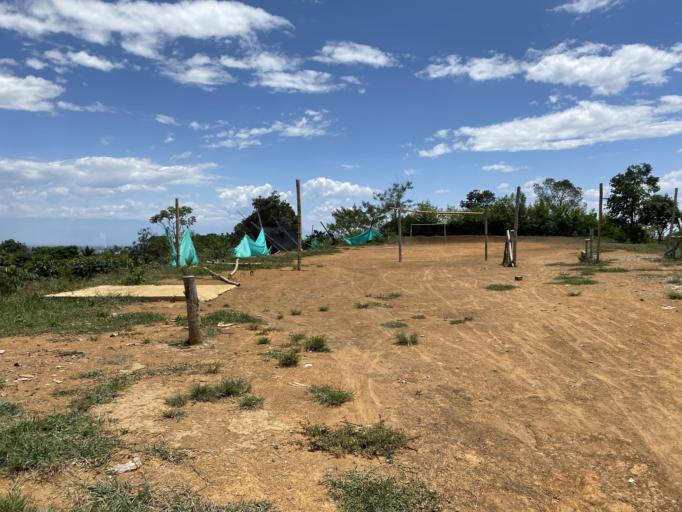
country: CO
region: Valle del Cauca
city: Jamundi
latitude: 3.2980
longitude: -76.5715
